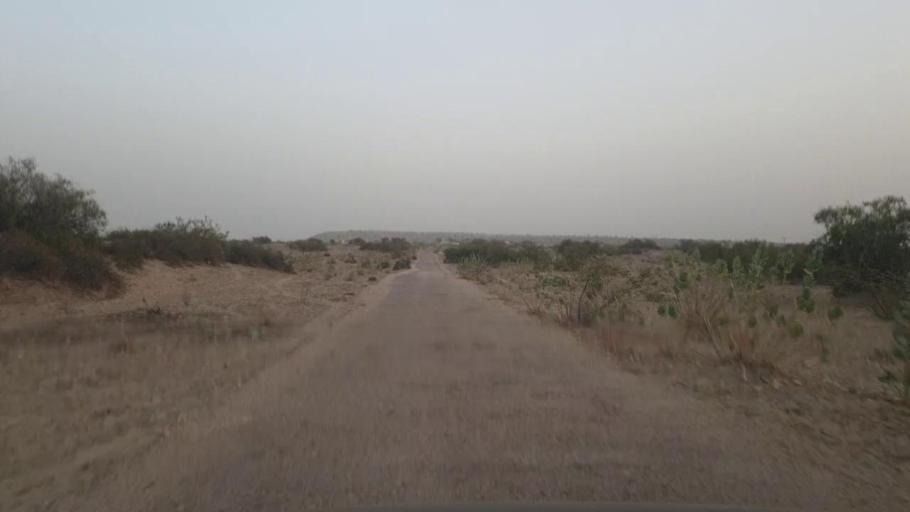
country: PK
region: Sindh
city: Chor
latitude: 25.5069
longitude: 69.8184
